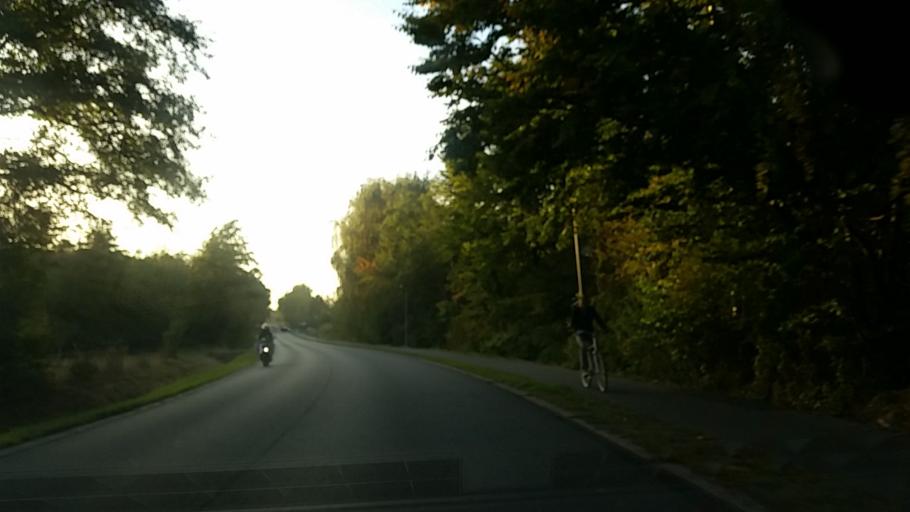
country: DE
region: Lower Saxony
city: Wolfsburg
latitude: 52.4204
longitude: 10.8400
